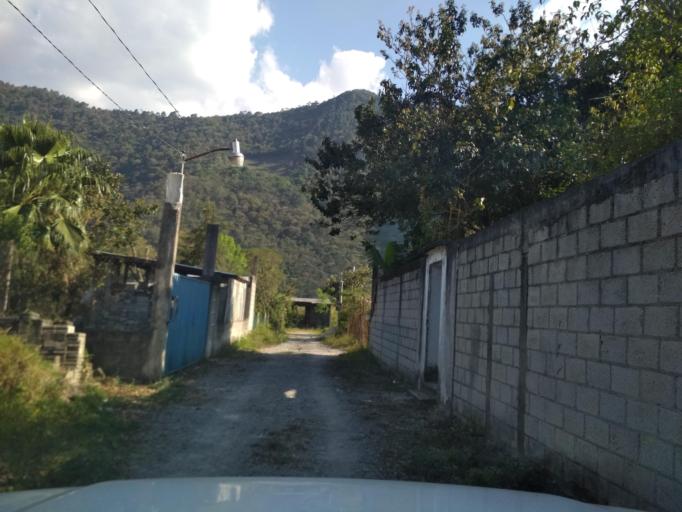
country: MX
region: Veracruz
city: Jalapilla
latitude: 18.8088
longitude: -97.0914
